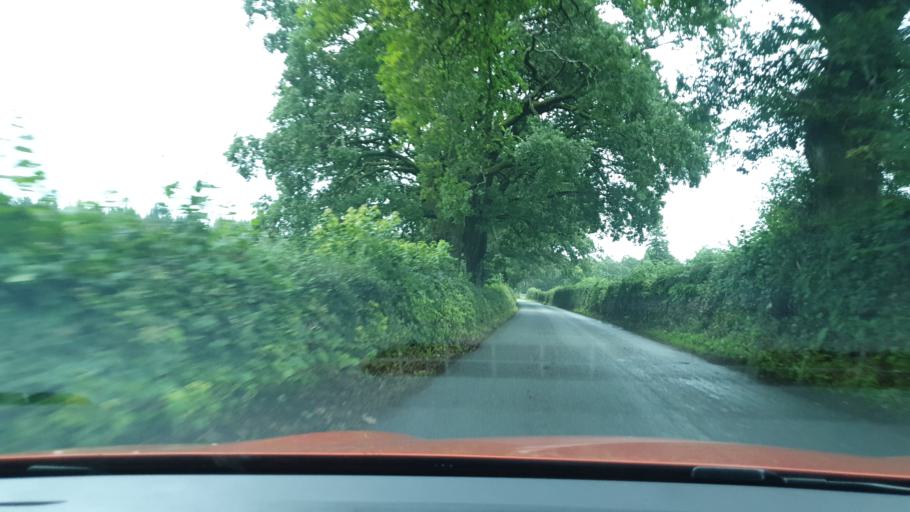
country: GB
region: England
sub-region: Cumbria
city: Seascale
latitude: 54.3964
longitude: -3.3451
